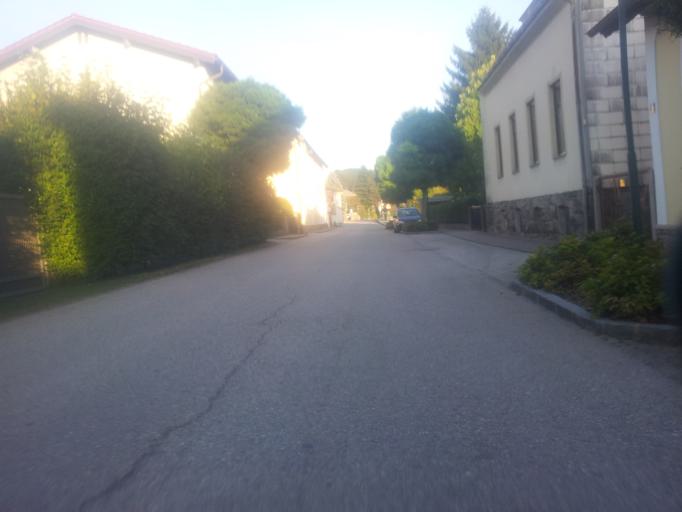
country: AT
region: Lower Austria
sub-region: Politischer Bezirk Lilienfeld
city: Hainfeld
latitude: 48.0375
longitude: 15.7694
